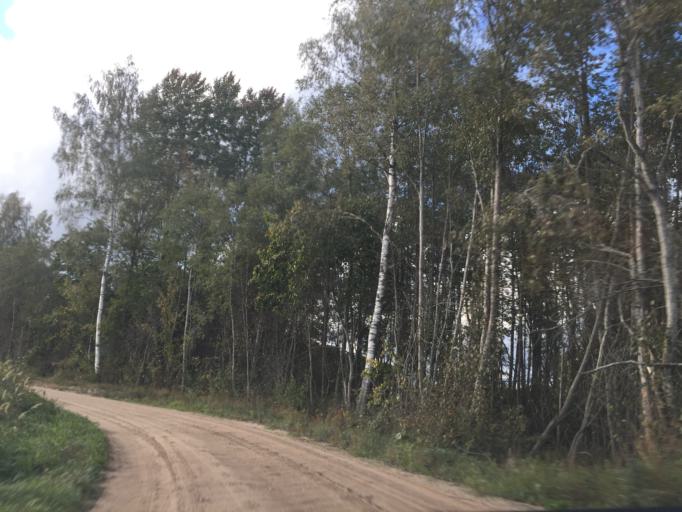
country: LV
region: Ligatne
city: Ligatne
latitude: 57.1349
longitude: 25.0979
